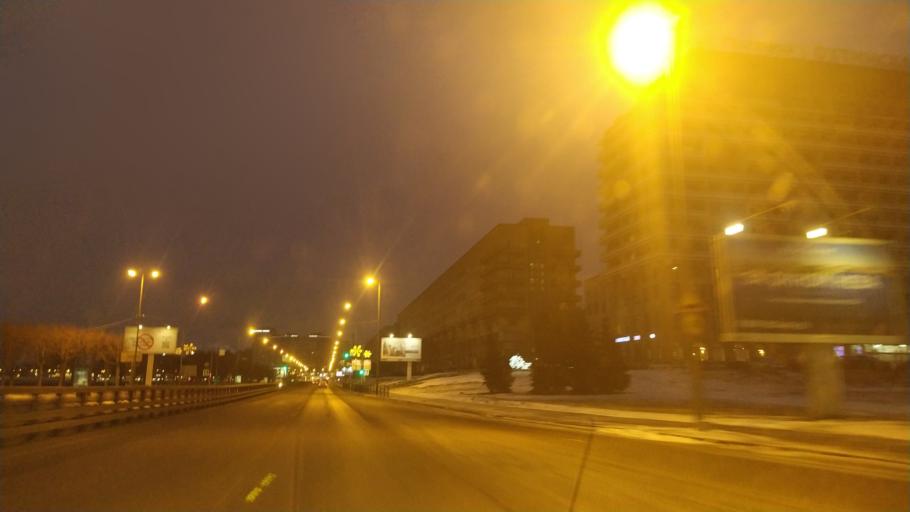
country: RU
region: Leningrad
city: Finlyandskiy
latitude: 59.9481
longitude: 30.4070
